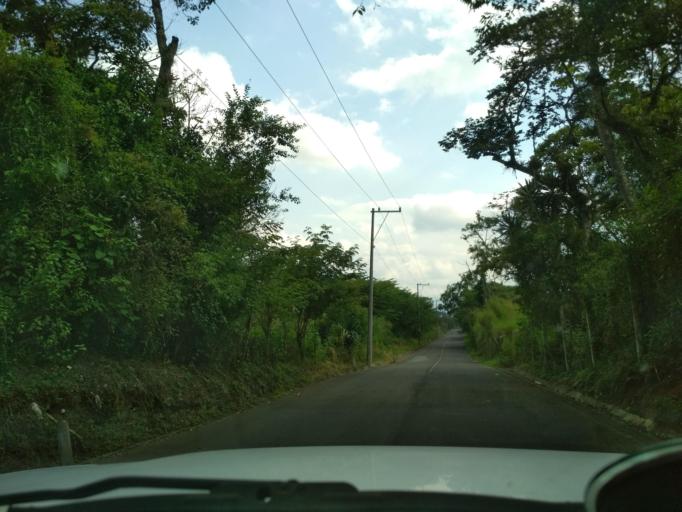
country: MX
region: Veracruz
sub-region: Ixtaczoquitlan
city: Buenavista
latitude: 18.9123
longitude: -97.0263
